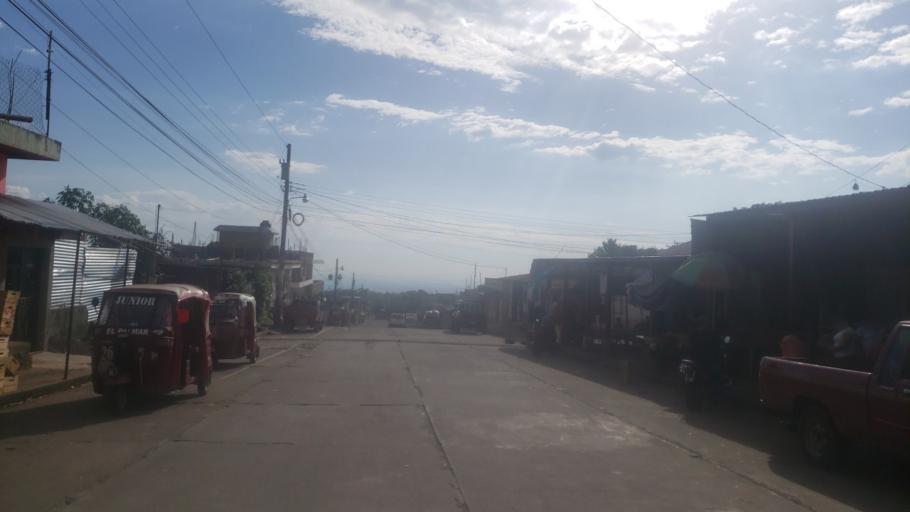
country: GT
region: Suchitepeque
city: Pueblo Nuevo
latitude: 14.6468
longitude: -91.5575
